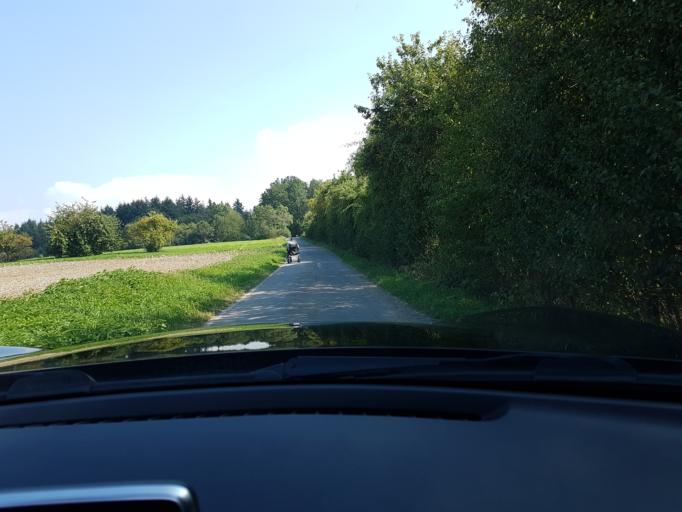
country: DE
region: Baden-Wuerttemberg
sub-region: Karlsruhe Region
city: Osterburken
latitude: 49.4283
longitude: 9.4516
